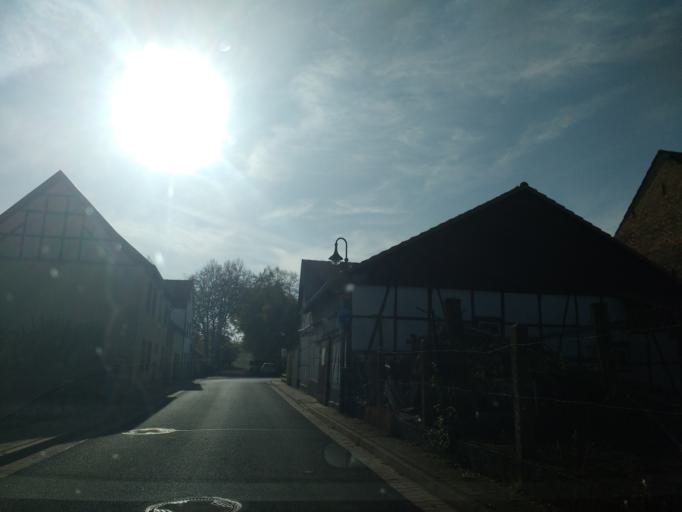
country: DE
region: Thuringia
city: Heroldishausen
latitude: 51.1379
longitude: 10.5174
